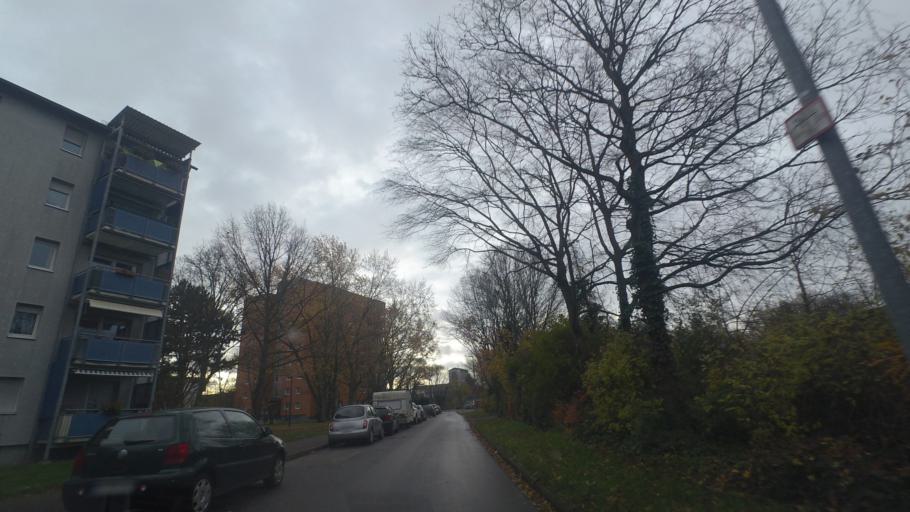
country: DE
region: Baden-Wuerttemberg
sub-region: Karlsruhe Region
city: Karlsruhe
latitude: 49.0149
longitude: 8.4377
